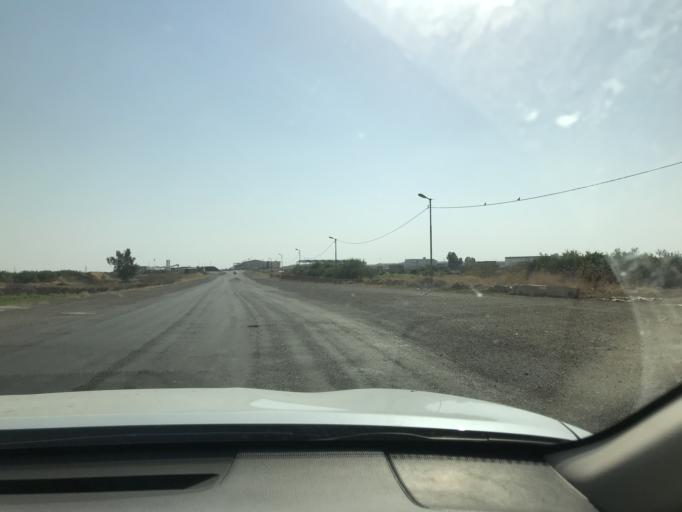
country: IQ
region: Arbil
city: Erbil
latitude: 36.1711
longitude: 43.9228
